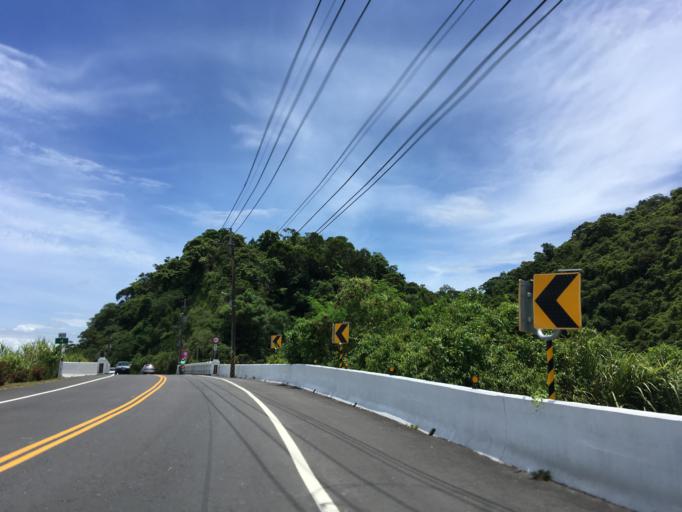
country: TW
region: Taiwan
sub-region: Yilan
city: Yilan
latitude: 24.6436
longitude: 121.7218
